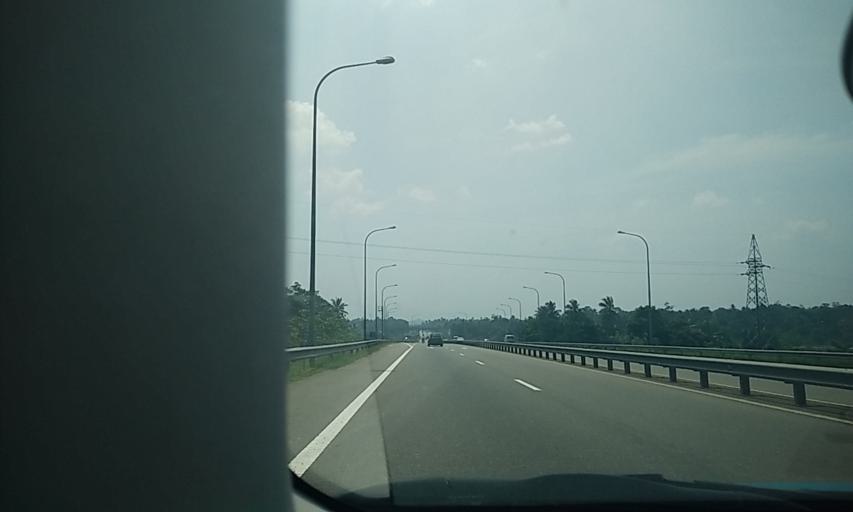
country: LK
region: Western
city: Horana South
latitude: 6.7183
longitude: 80.0000
